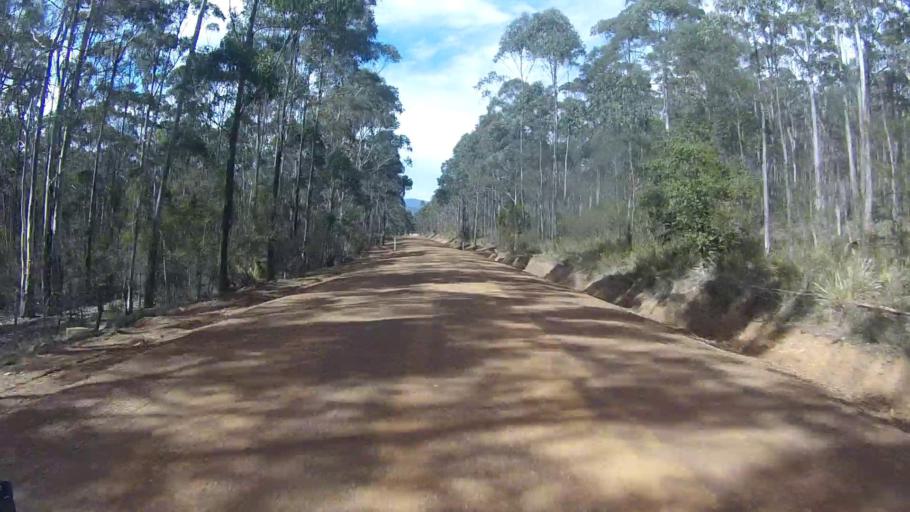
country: AU
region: Tasmania
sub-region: Sorell
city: Sorell
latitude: -42.6252
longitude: 147.9026
